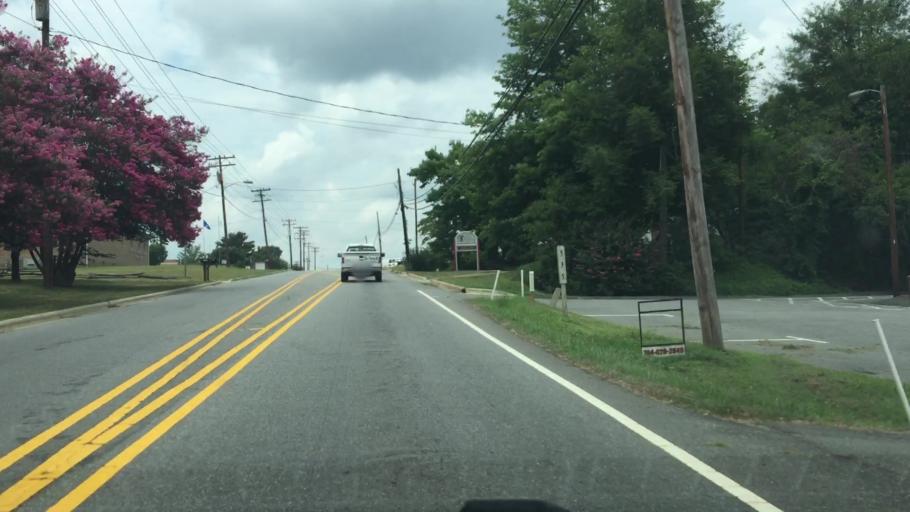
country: US
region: North Carolina
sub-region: Iredell County
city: Troutman
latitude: 35.6990
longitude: -80.8824
